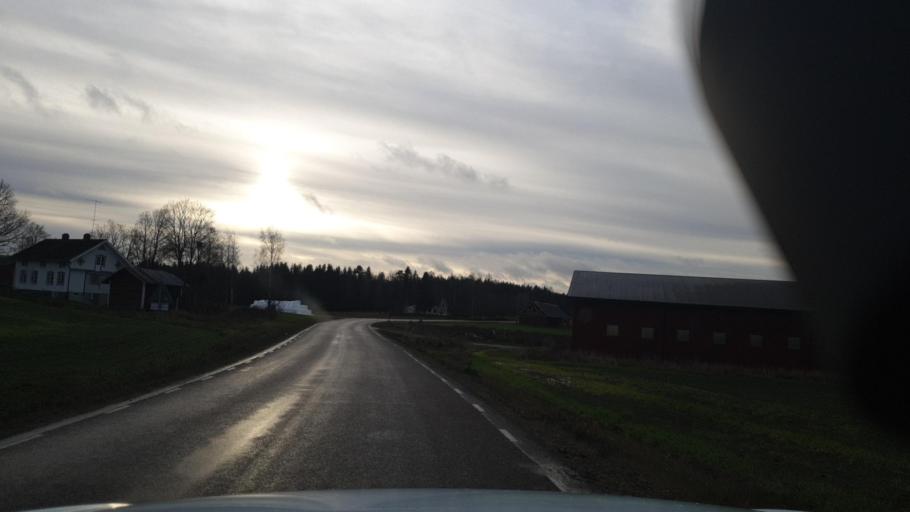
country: SE
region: Vaermland
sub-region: Eda Kommun
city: Charlottenberg
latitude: 59.7685
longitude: 12.1608
